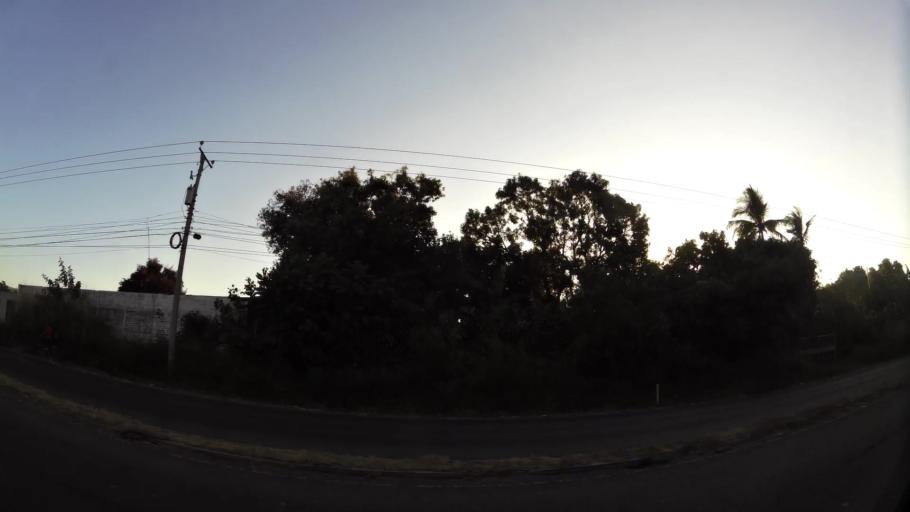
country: SV
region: Sonsonate
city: Armenia
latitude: 13.7318
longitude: -89.3854
